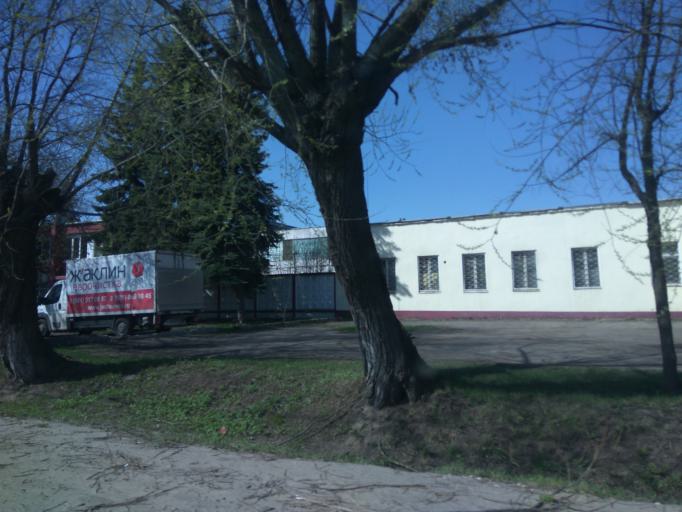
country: RU
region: Moskovskaya
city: Ramenskoye
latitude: 55.5640
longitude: 38.2634
